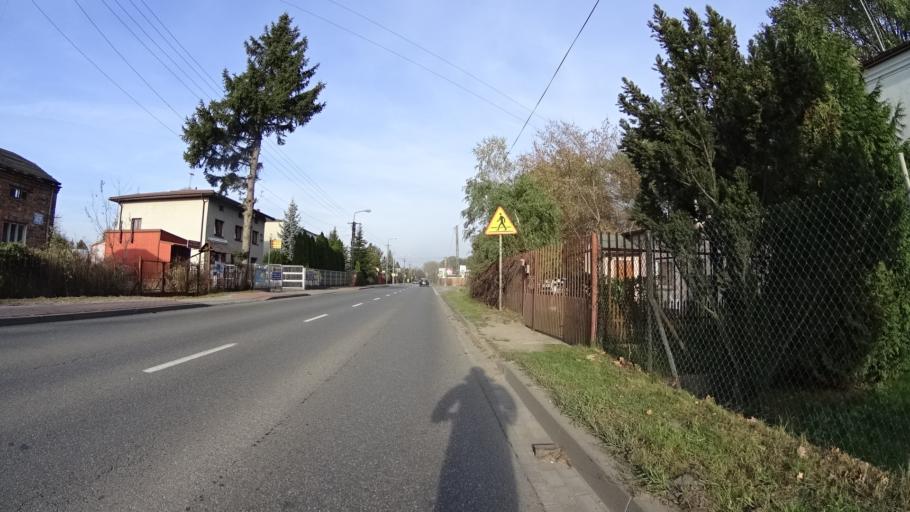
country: PL
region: Masovian Voivodeship
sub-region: Powiat warszawski zachodni
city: Babice
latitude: 52.2574
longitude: 20.8510
